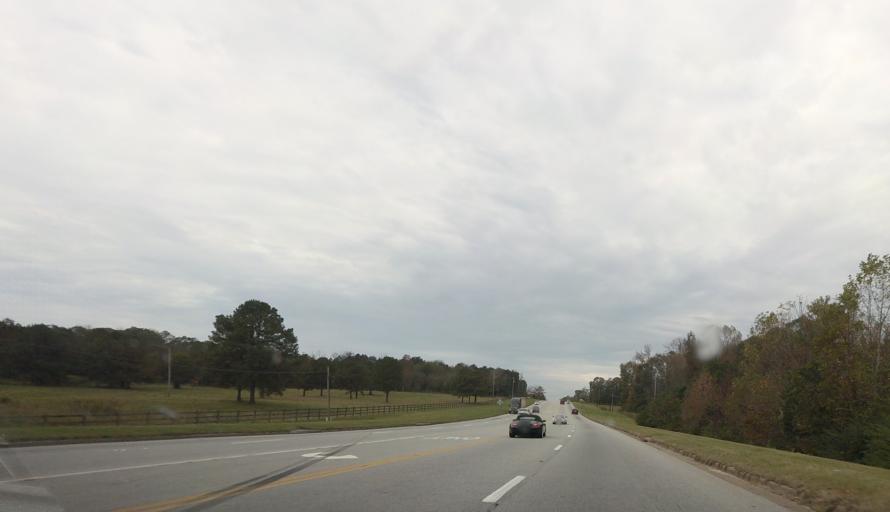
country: US
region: Alabama
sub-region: Lee County
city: Opelika
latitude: 32.6407
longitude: -85.3167
